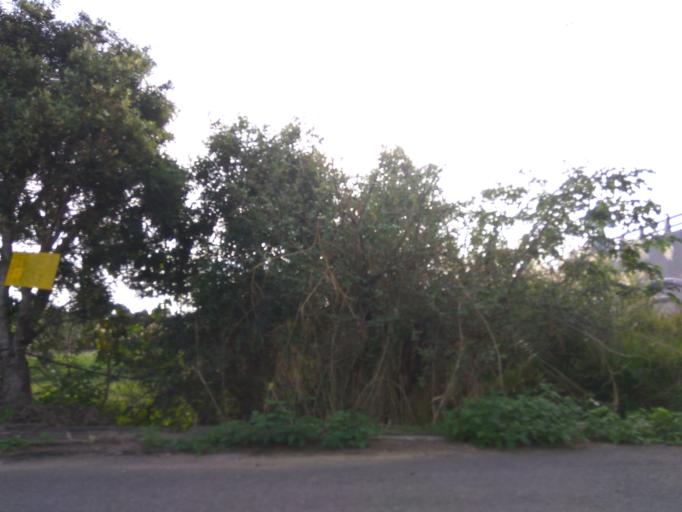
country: TW
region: Taiwan
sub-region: Hsinchu
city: Zhubei
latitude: 24.9427
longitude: 120.9903
